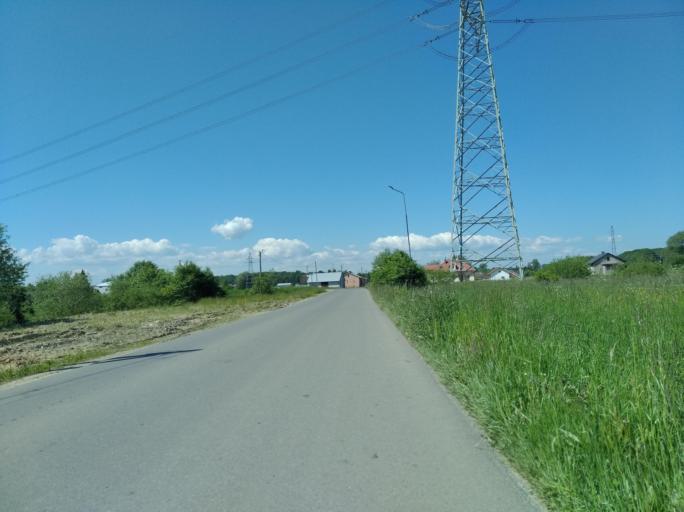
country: PL
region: Subcarpathian Voivodeship
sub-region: Powiat krosnienski
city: Odrzykon
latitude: 49.7349
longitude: 21.7205
